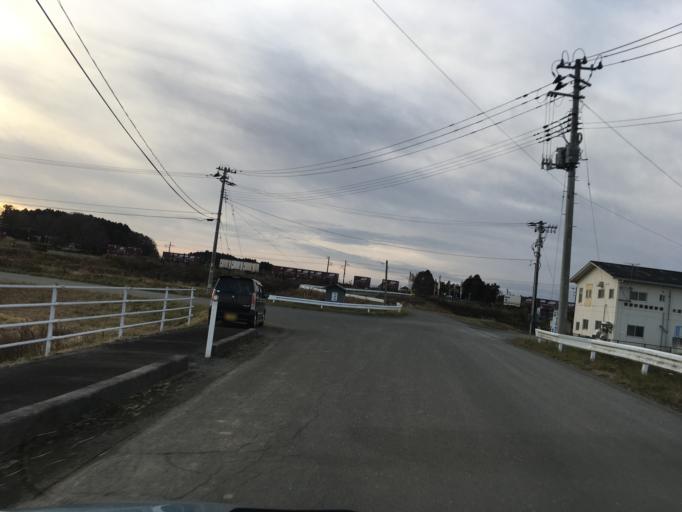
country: JP
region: Miyagi
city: Kogota
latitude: 38.6387
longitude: 141.0701
